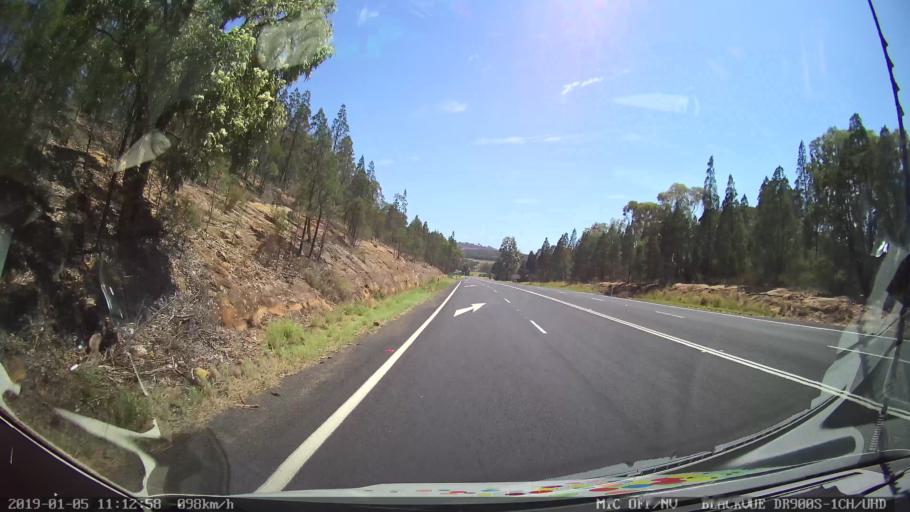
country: AU
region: New South Wales
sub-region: Warrumbungle Shire
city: Coonabarabran
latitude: -31.3761
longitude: 149.2663
